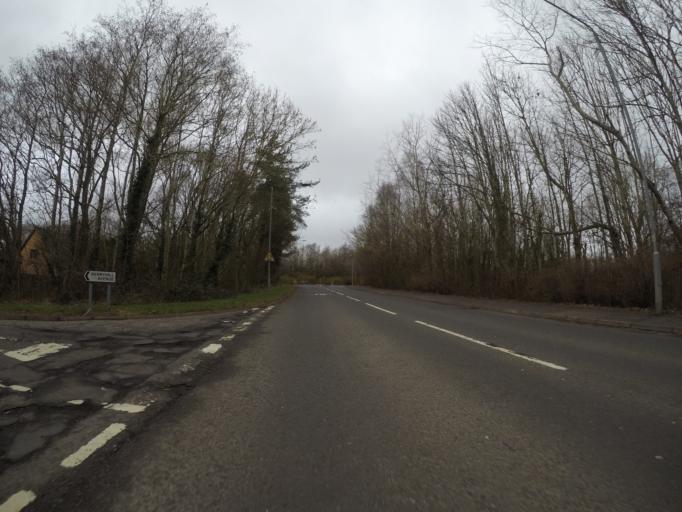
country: GB
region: Scotland
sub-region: North Ayrshire
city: Springside
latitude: 55.6316
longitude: -4.6256
